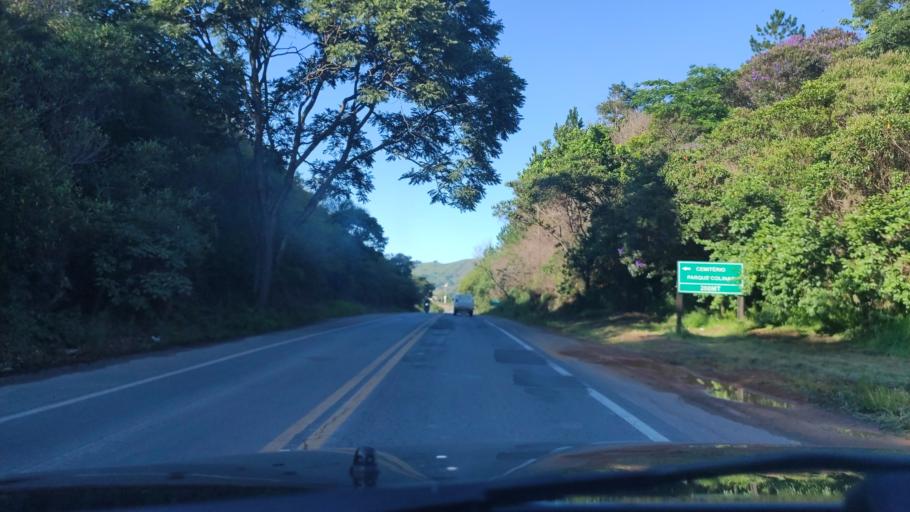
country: BR
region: Sao Paulo
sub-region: Socorro
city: Socorro
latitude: -22.6007
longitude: -46.5216
